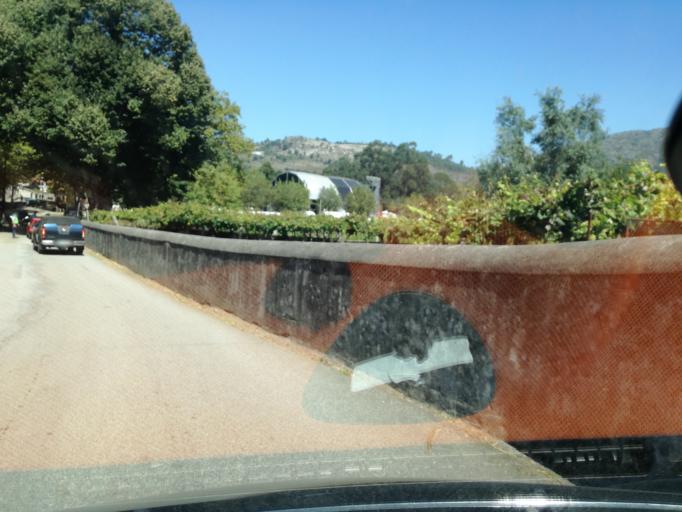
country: ES
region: Galicia
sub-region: Provincia de Pontevedra
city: O Rosal
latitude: 41.8860
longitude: -8.7876
